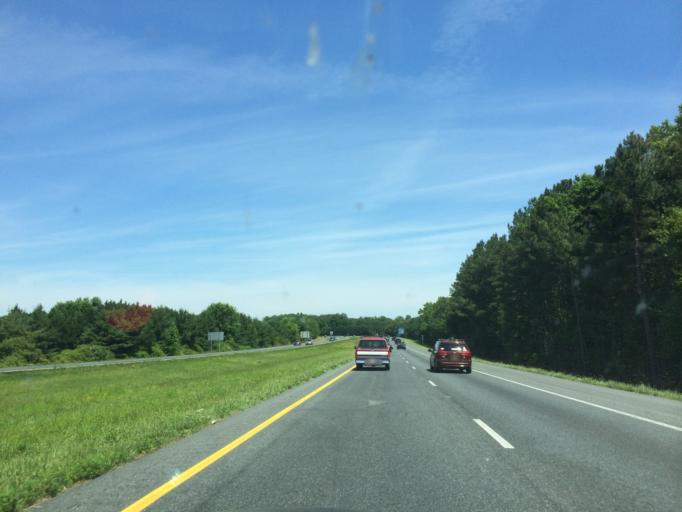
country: US
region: Maryland
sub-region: Wicomico County
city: Salisbury
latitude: 38.3828
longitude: -75.5405
